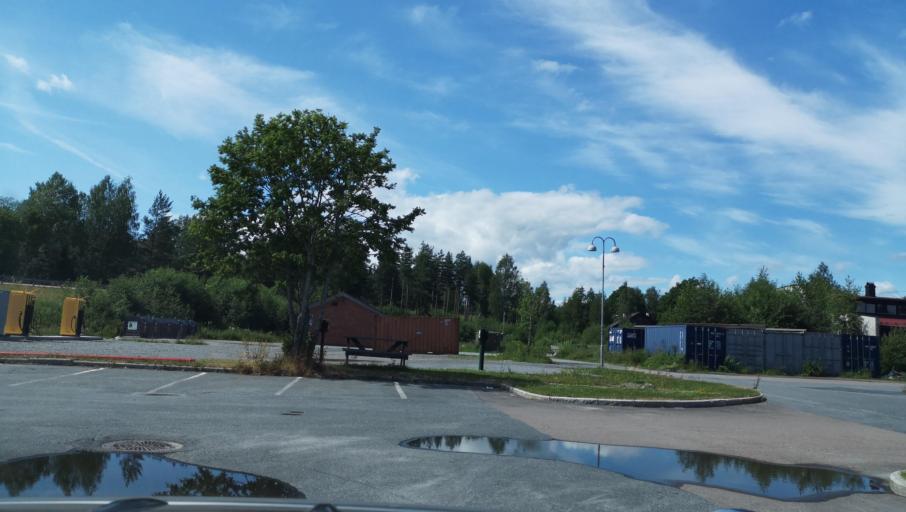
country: NO
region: Buskerud
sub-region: Modum
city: Vikersund
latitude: 59.9641
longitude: 9.9930
